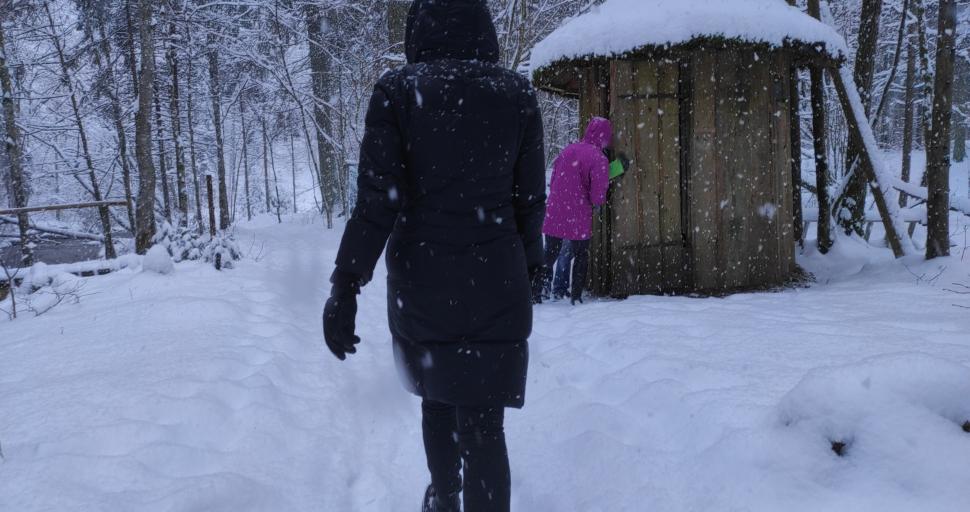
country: LV
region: Amatas Novads
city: Drabesi
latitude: 57.2197
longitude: 25.1622
